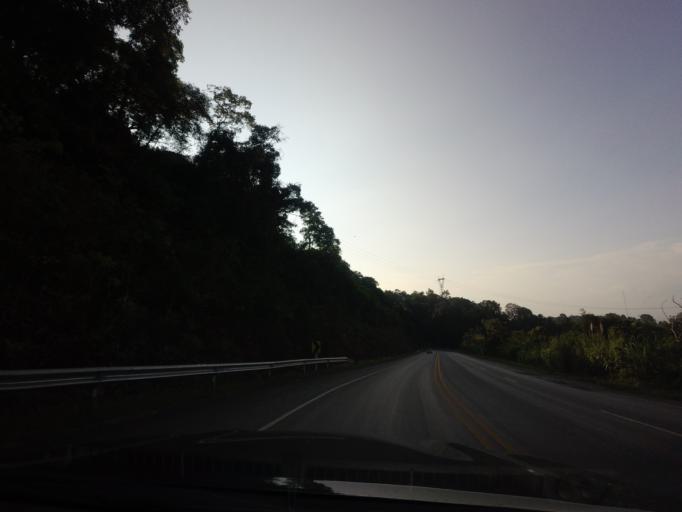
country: TH
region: Loei
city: Dan Sai
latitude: 17.2274
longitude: 101.1511
